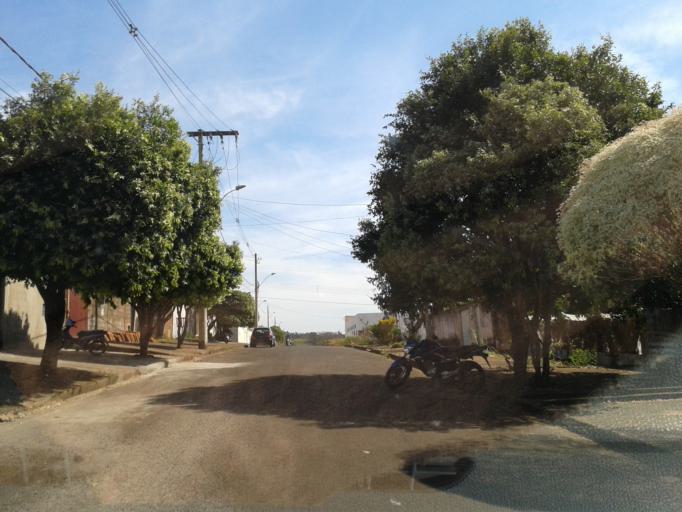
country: BR
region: Minas Gerais
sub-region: Ituiutaba
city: Ituiutaba
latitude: -18.9616
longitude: -49.4637
